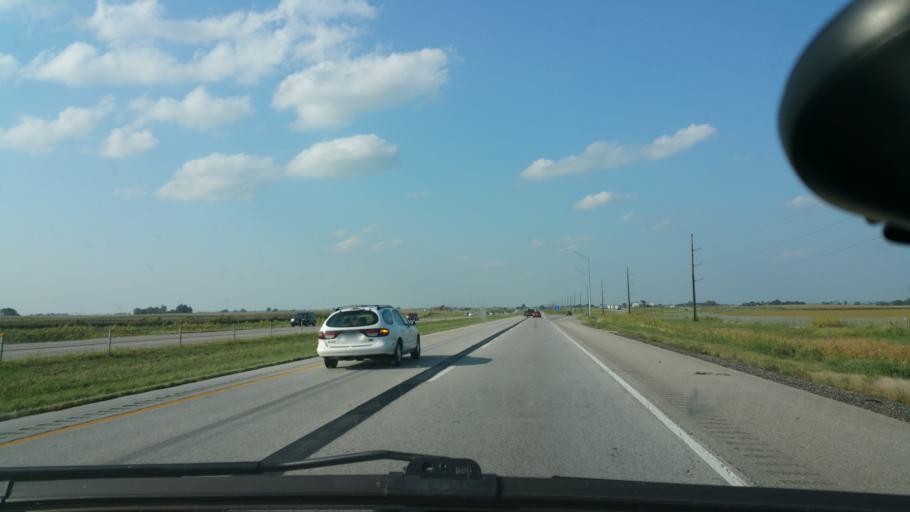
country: US
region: Iowa
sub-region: Story County
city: Huxley
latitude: 41.8214
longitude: -93.5706
